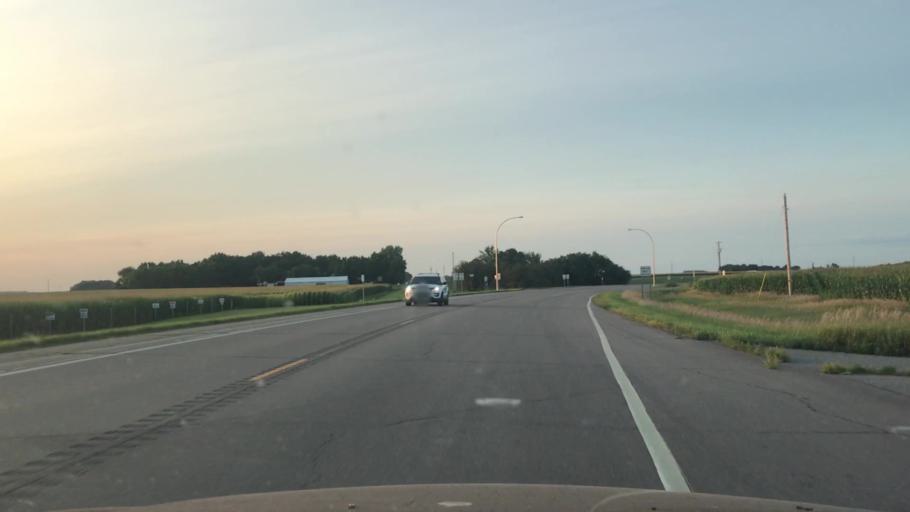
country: US
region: Minnesota
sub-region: Redwood County
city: Redwood Falls
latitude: 44.4116
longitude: -95.1276
